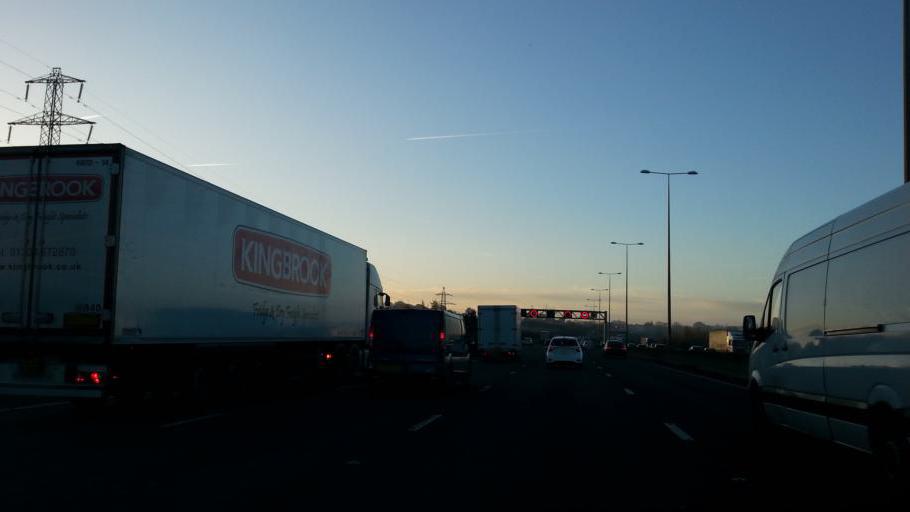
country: GB
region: England
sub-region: Hertfordshire
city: Redbourn
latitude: 51.7932
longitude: -0.4117
